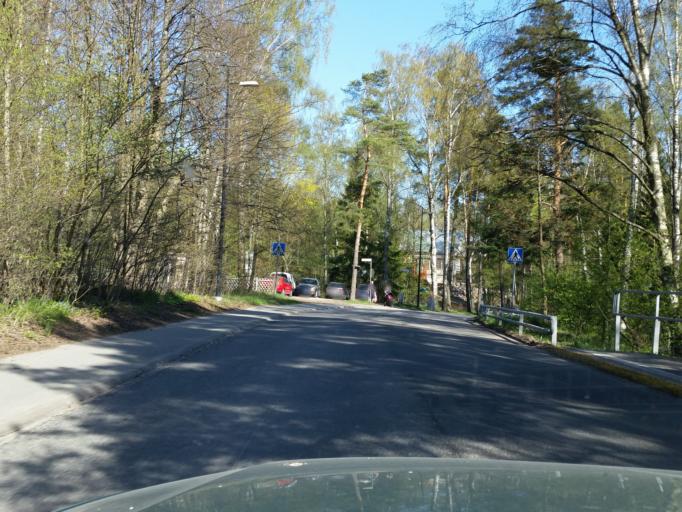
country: FI
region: Uusimaa
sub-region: Helsinki
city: Helsinki
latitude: 60.1884
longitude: 24.8894
